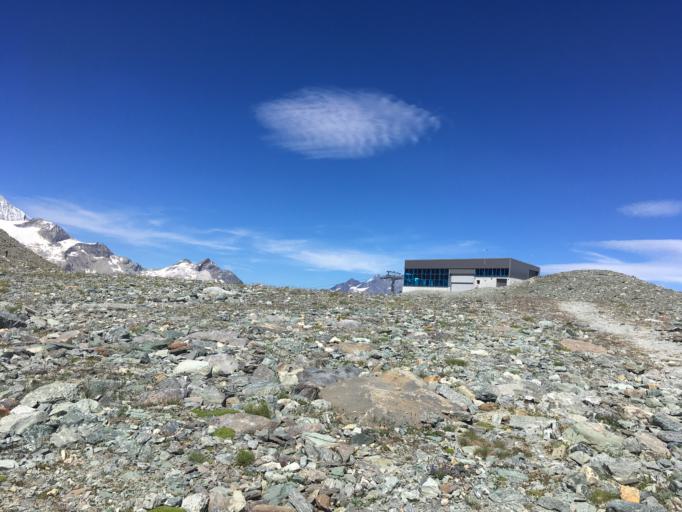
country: CH
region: Valais
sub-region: Visp District
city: Zermatt
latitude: 45.9882
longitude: 7.6974
